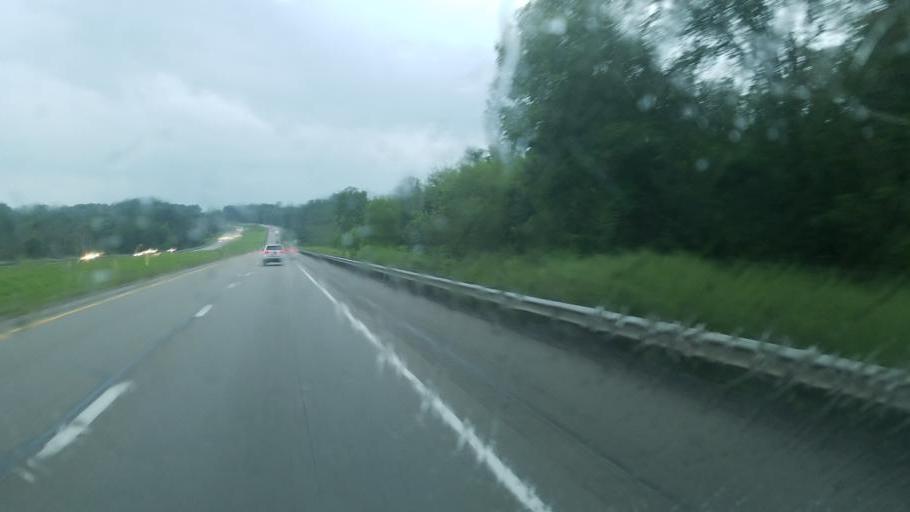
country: US
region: Pennsylvania
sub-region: Mercer County
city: Grove City
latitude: 41.1901
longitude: -80.1640
